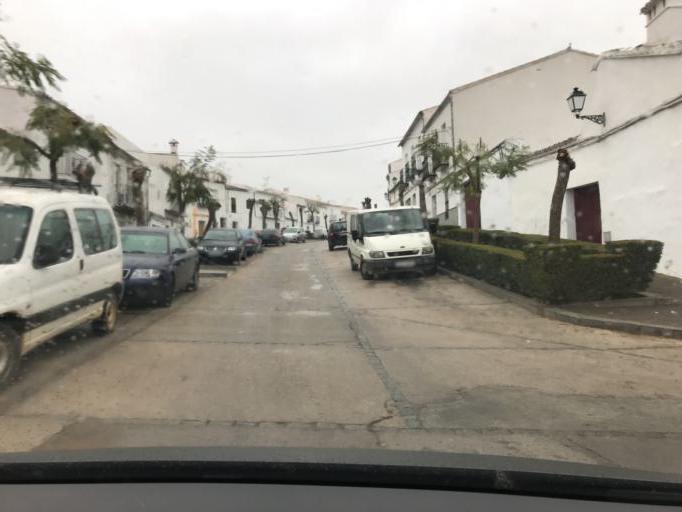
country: ES
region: Andalusia
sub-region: Provincia de Sevilla
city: Guadalcanal
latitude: 38.0957
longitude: -5.8180
